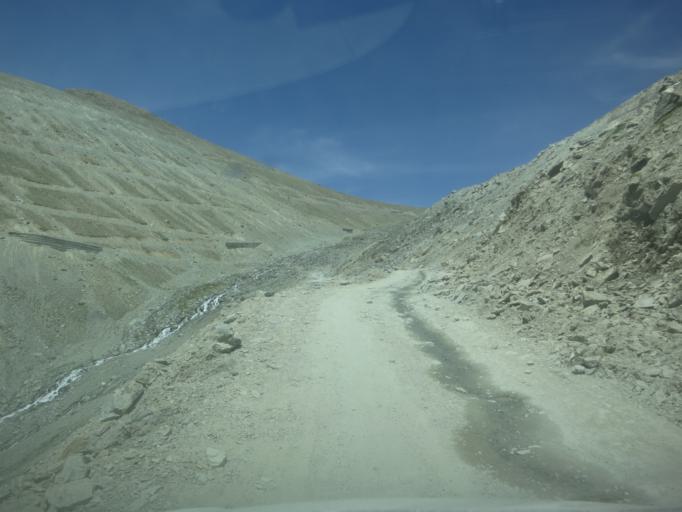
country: IN
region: Himachal Pradesh
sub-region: Kulu
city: Manali
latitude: 32.3847
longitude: 77.6187
